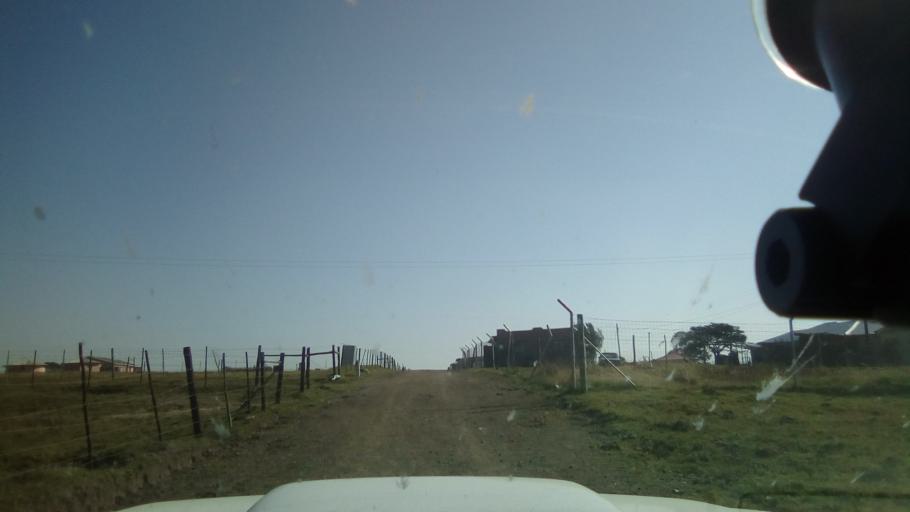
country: ZA
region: Eastern Cape
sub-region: Buffalo City Metropolitan Municipality
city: Bhisho
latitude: -32.9487
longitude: 27.3240
